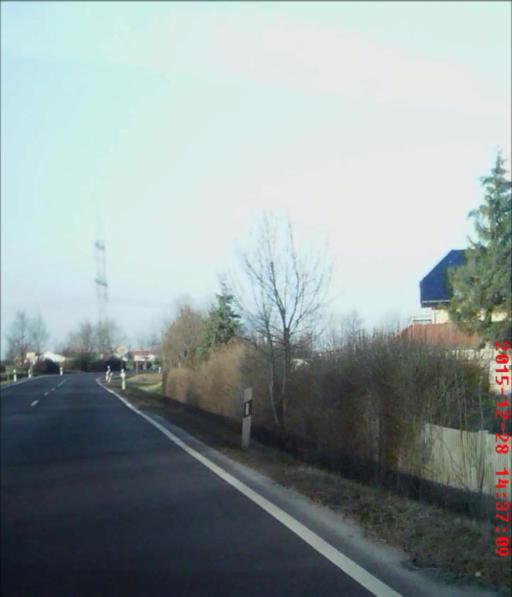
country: DE
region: Thuringia
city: Buttelstedt
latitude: 51.0633
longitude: 11.3413
